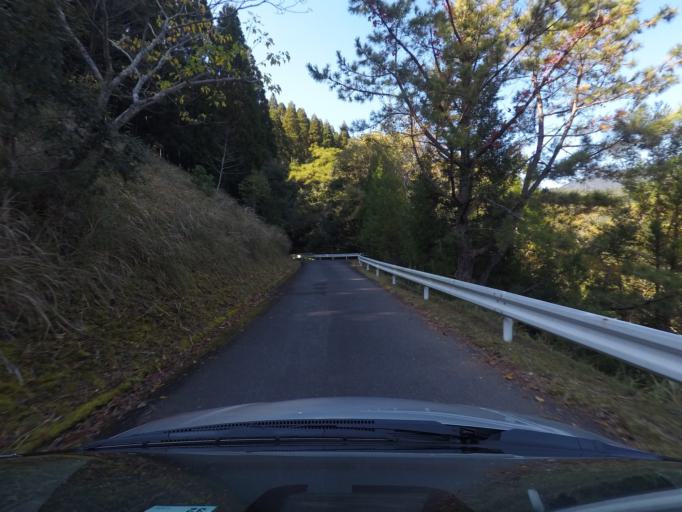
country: JP
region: Miyazaki
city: Kobayashi
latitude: 32.0231
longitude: 131.1820
